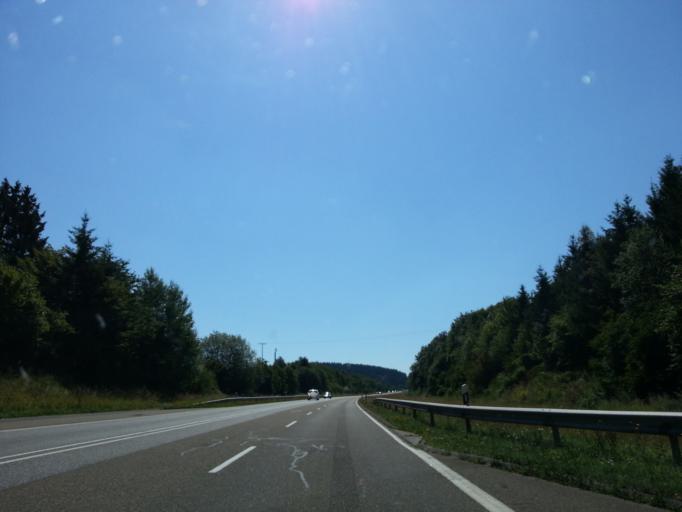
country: DE
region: Rheinland-Pfalz
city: Grosslangenfeld
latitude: 50.2156
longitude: 6.2362
